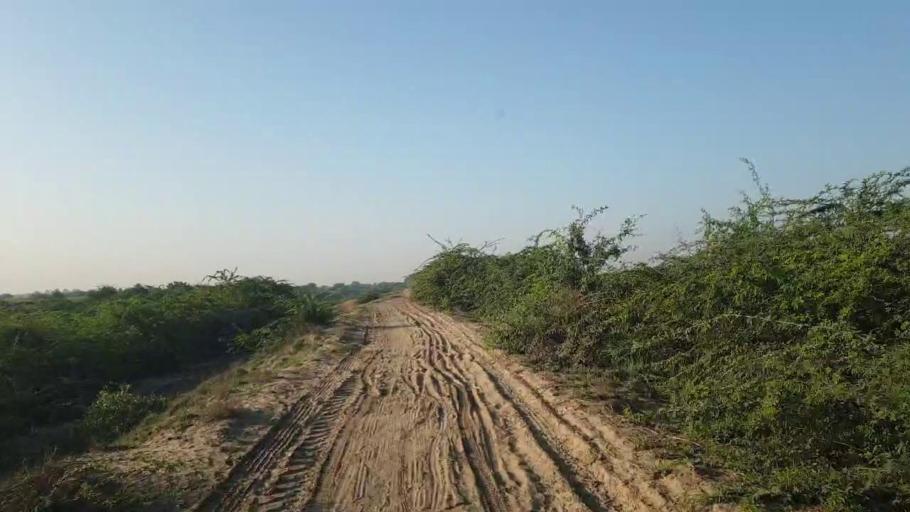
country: PK
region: Sindh
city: Badin
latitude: 24.6143
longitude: 68.7858
